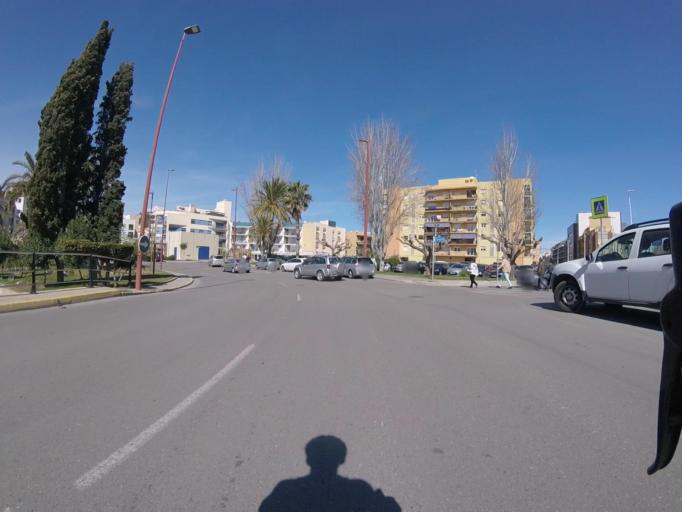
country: ES
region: Valencia
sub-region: Provincia de Castello
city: Peniscola
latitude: 40.3589
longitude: 0.3999
